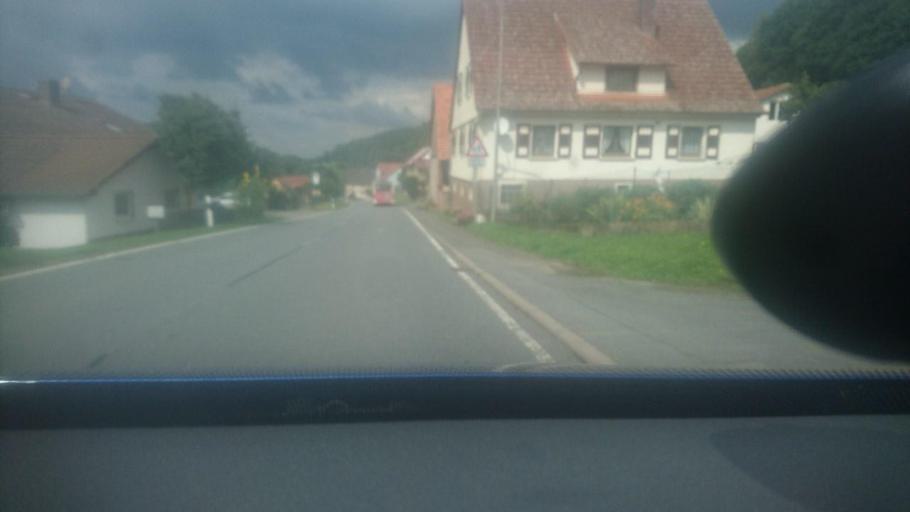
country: DE
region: Hesse
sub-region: Regierungsbezirk Darmstadt
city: Frankisch-Crumbach
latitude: 49.7192
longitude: 8.9112
